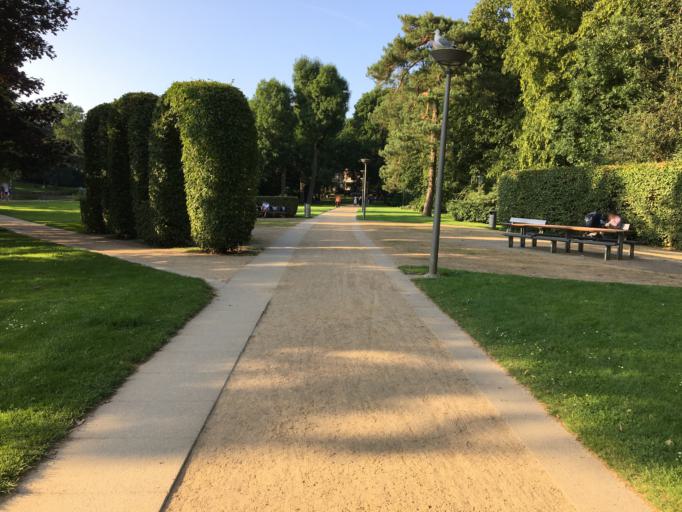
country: DE
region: Schleswig-Holstein
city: Travemuende
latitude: 53.9664
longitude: 10.8776
